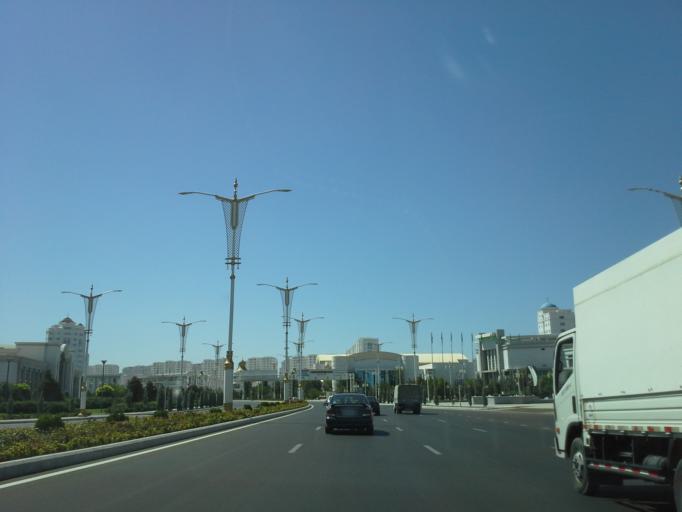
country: TM
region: Ahal
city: Ashgabat
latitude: 37.9146
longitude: 58.3774
